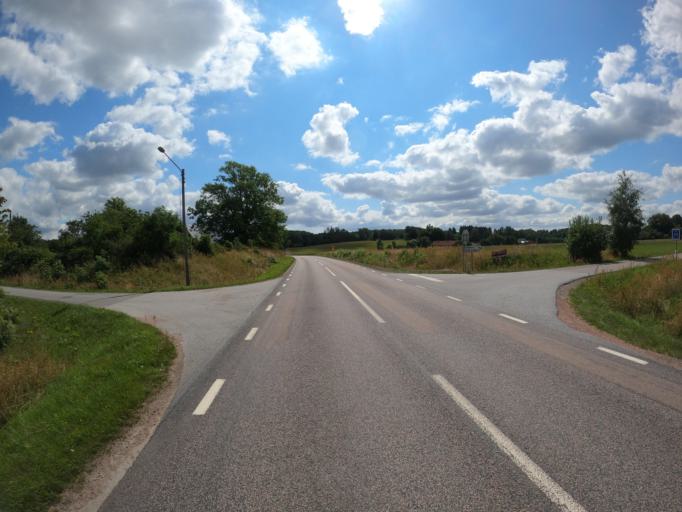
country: SE
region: Skane
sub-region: Lunds Kommun
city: Veberod
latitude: 55.5931
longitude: 13.4932
